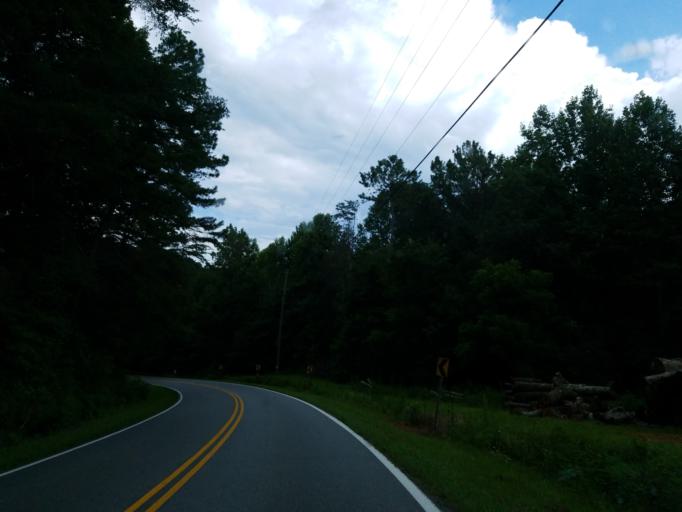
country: US
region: Georgia
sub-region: Gilmer County
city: Ellijay
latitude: 34.6707
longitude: -84.3672
